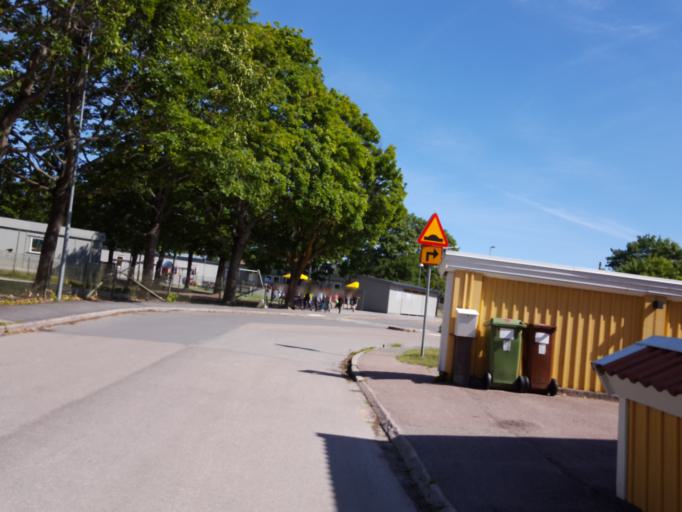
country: SE
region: Uppsala
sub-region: Uppsala Kommun
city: Uppsala
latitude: 59.8623
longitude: 17.6642
